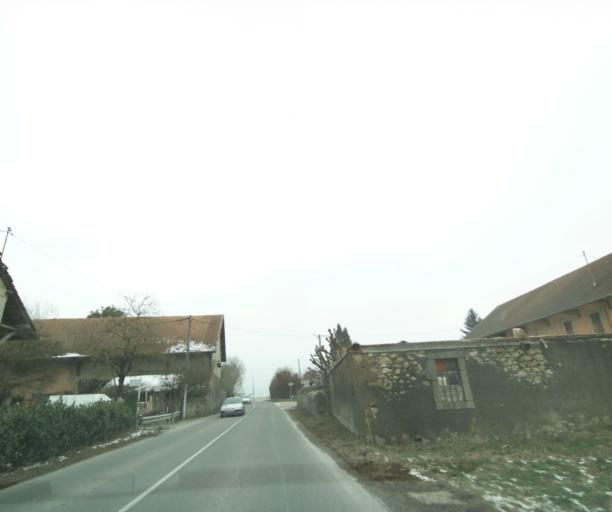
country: FR
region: Rhone-Alpes
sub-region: Departement de la Haute-Savoie
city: Reignier-Esery
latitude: 46.1378
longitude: 6.2880
